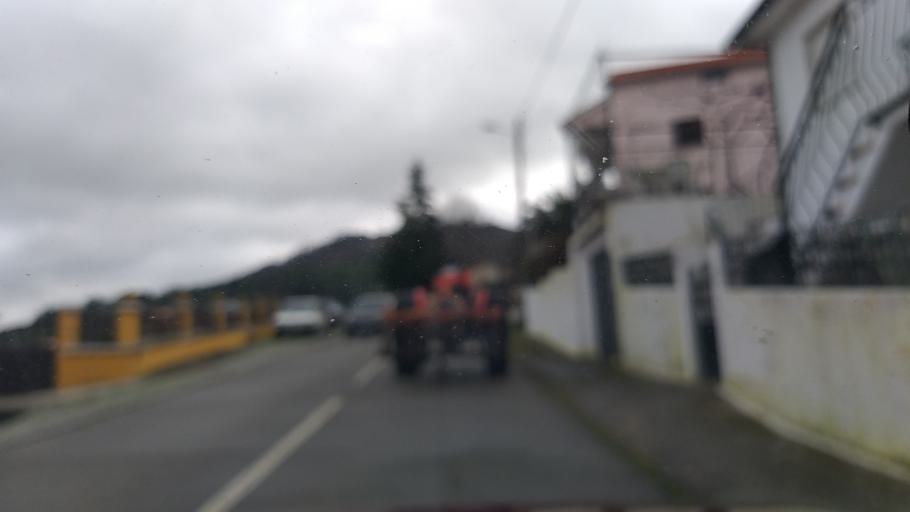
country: PT
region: Guarda
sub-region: Celorico da Beira
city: Celorico da Beira
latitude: 40.7105
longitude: -7.4337
